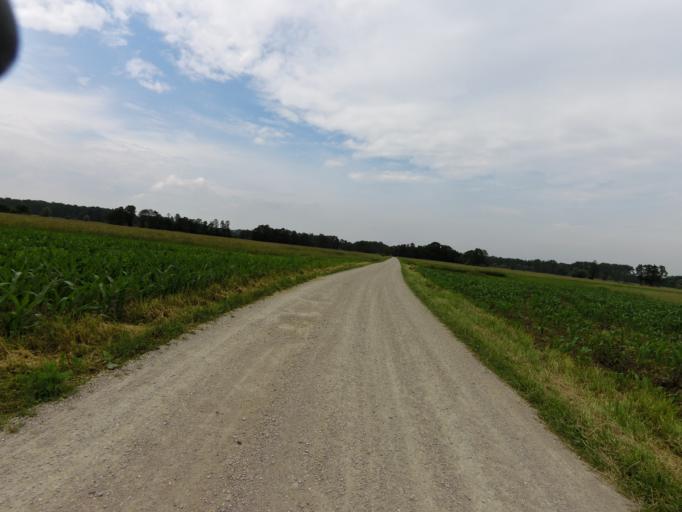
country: DE
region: Bavaria
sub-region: Upper Bavaria
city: Langenbach
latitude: 48.4529
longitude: 11.8871
